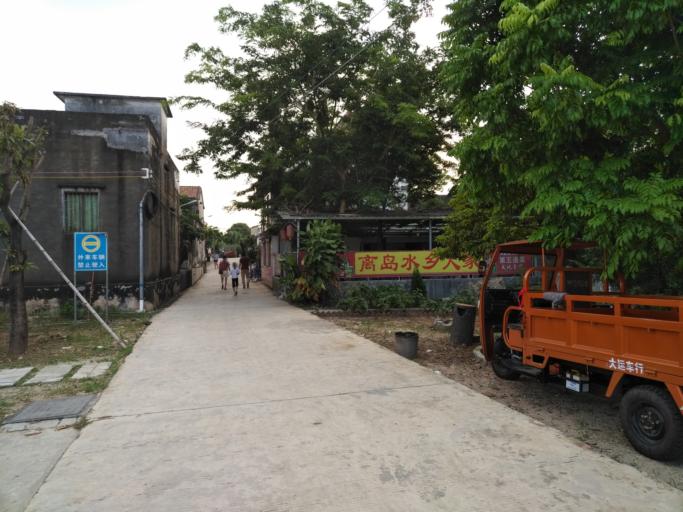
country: CN
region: Guangdong
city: Da'ao
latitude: 22.4539
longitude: 113.2107
